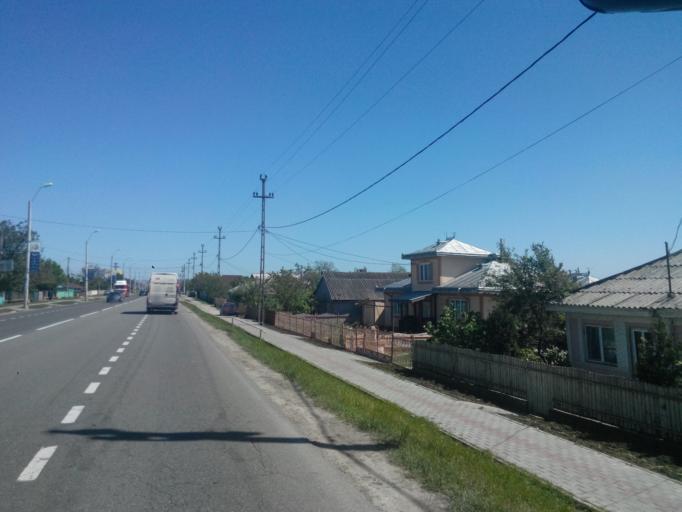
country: RO
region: Iasi
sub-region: Comuna Letcani
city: Letcani
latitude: 47.1941
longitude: 27.4192
